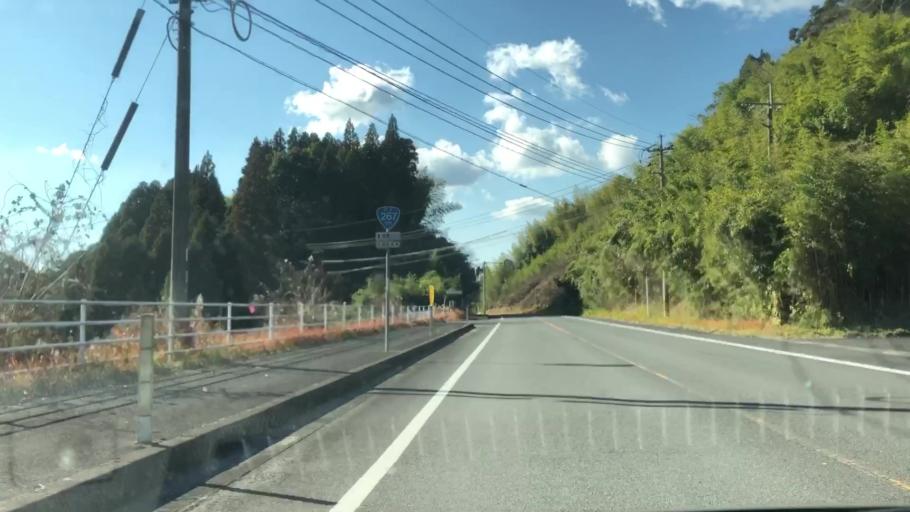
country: JP
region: Kagoshima
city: Satsumasendai
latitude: 31.8626
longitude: 130.3980
